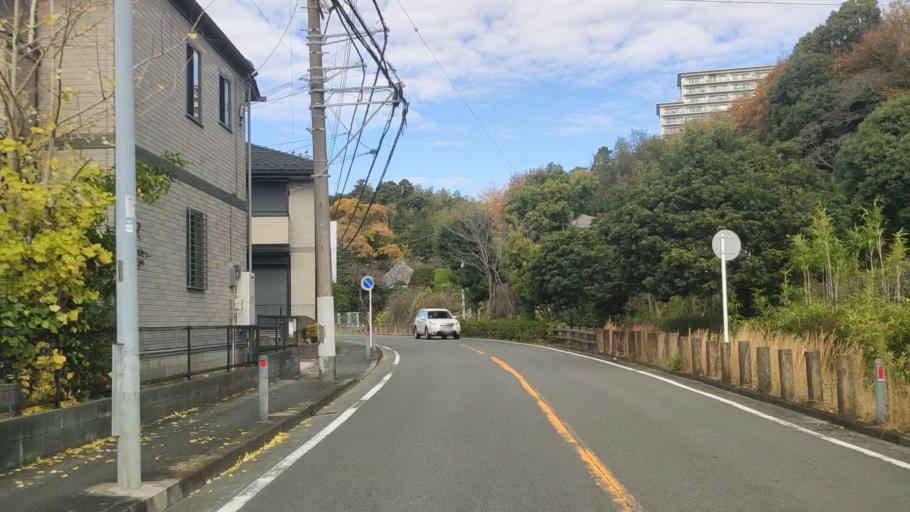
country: JP
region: Kanagawa
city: Yokohama
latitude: 35.4349
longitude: 139.5465
